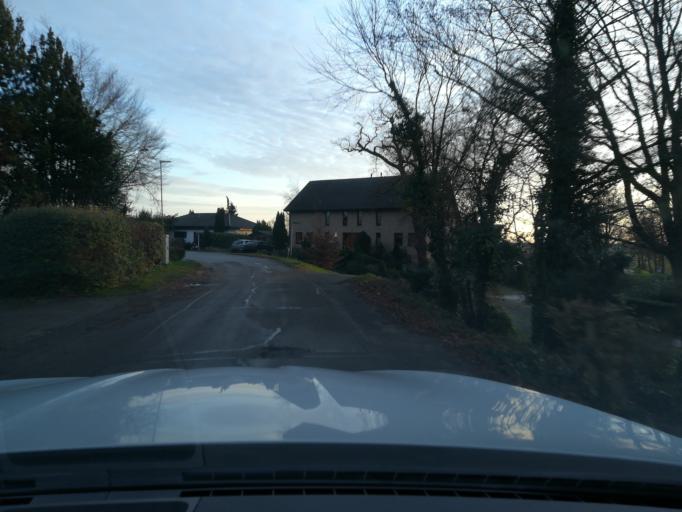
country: DE
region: Lower Saxony
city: Stelle
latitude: 53.4414
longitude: 10.0820
